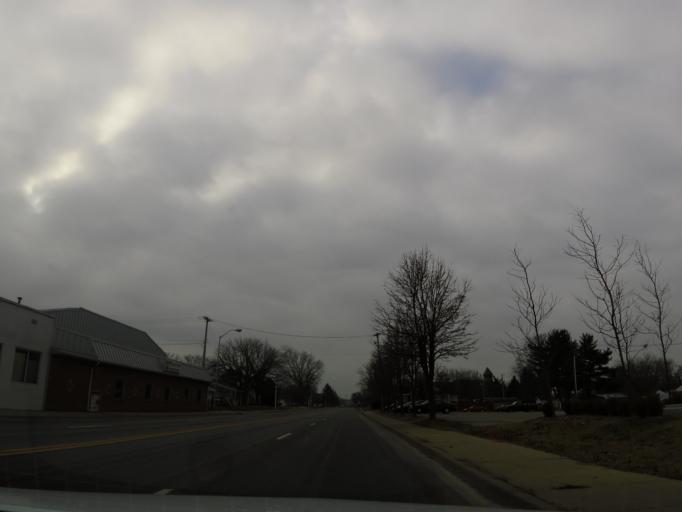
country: US
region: Indiana
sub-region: Bartholomew County
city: Columbus
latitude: 39.2136
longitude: -85.9042
